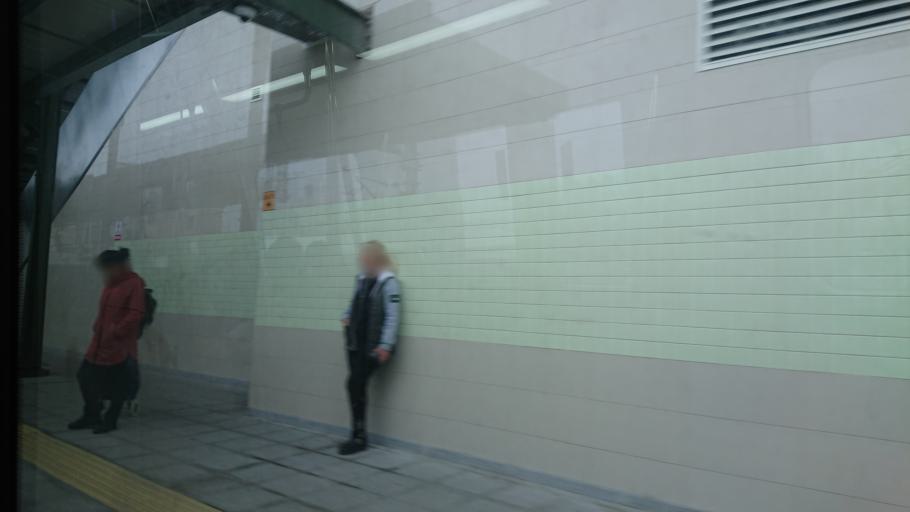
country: TR
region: Istanbul
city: Mahmutbey
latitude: 40.9887
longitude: 28.7729
